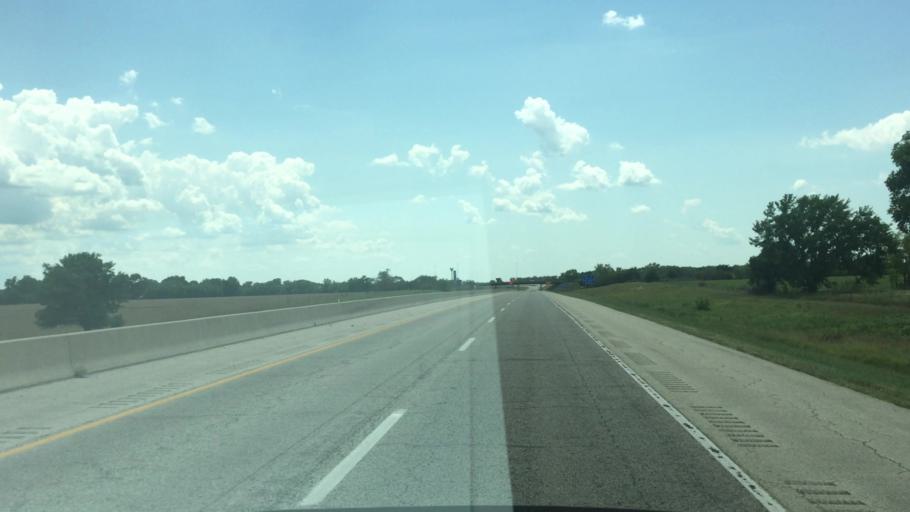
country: US
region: Kansas
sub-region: Lyon County
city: Emporia
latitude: 38.4818
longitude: -96.1744
